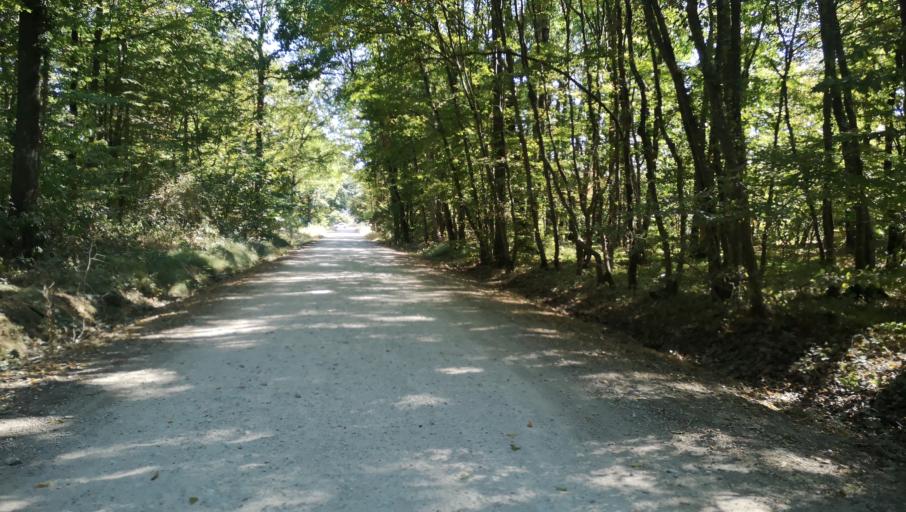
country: FR
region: Centre
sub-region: Departement du Loiret
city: Saran
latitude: 47.9594
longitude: 1.8956
